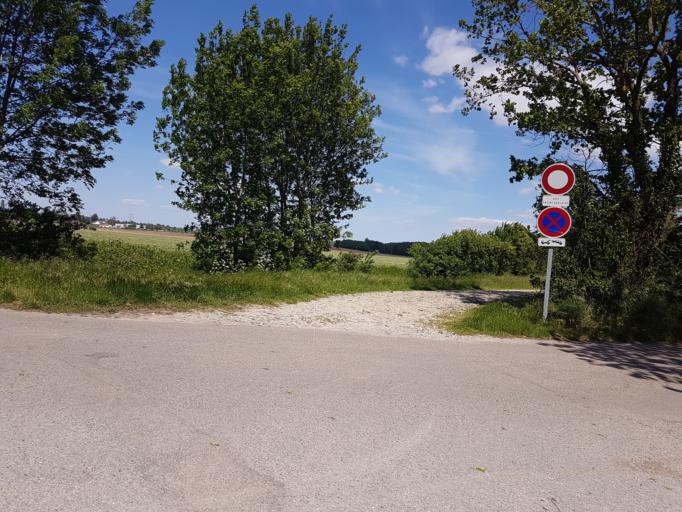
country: FR
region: Rhone-Alpes
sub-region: Departement du Rhone
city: Jonage
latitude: 45.7919
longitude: 5.0594
